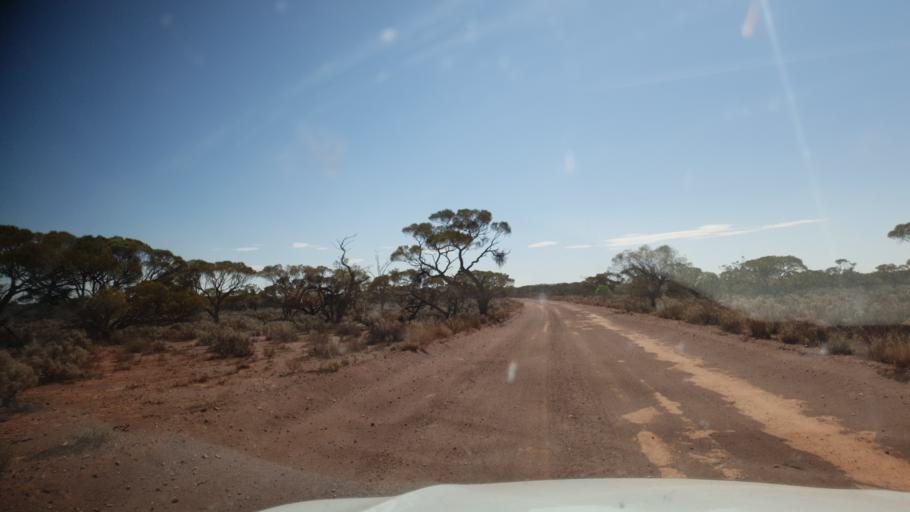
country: AU
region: South Australia
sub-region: Kimba
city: Caralue
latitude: -32.4902
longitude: 136.0671
